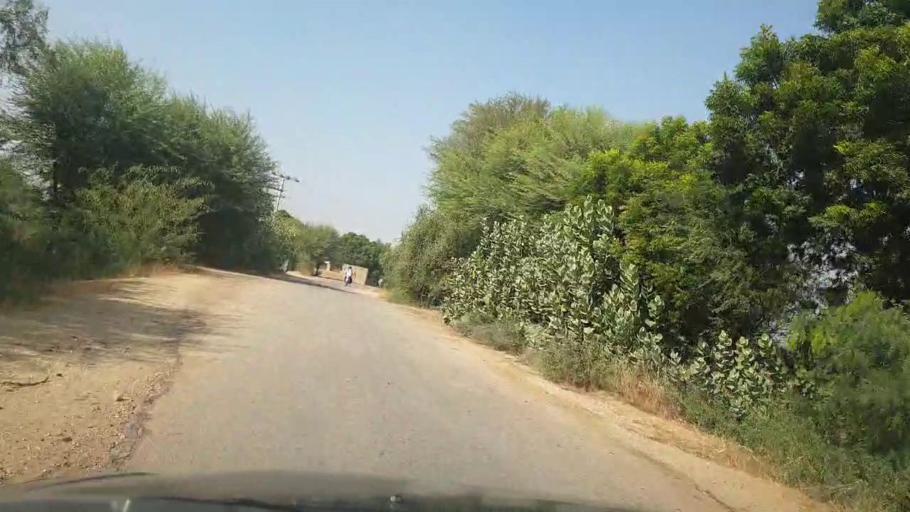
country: PK
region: Sindh
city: Jamshoro
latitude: 25.5259
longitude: 67.8218
